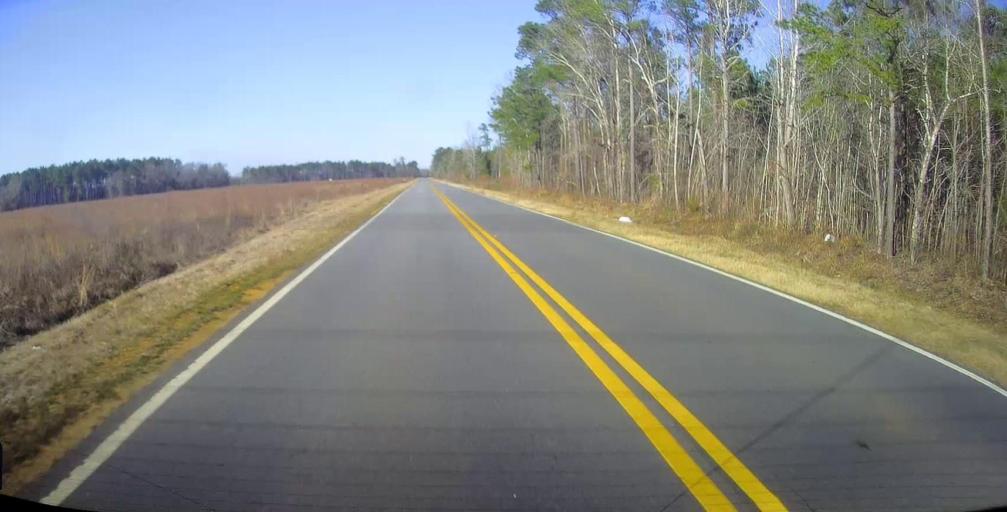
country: US
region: Georgia
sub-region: Sumter County
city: Americus
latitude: 32.1030
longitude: -84.1663
